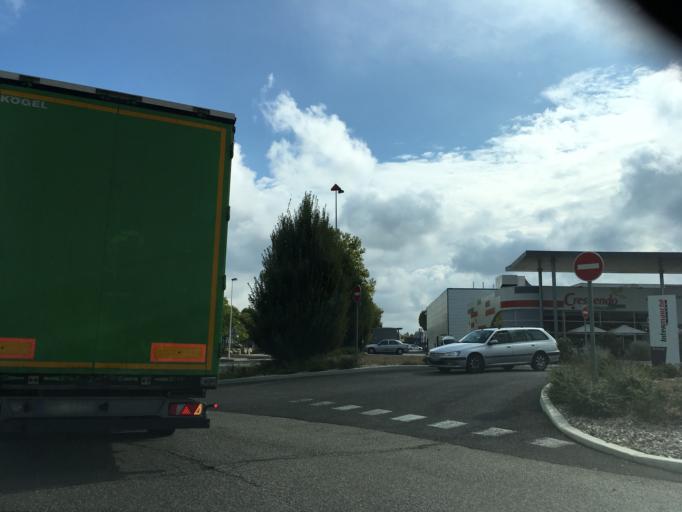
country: FR
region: Aquitaine
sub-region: Departement du Lot-et-Garonne
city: Agen
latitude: 44.1827
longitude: 0.6188
